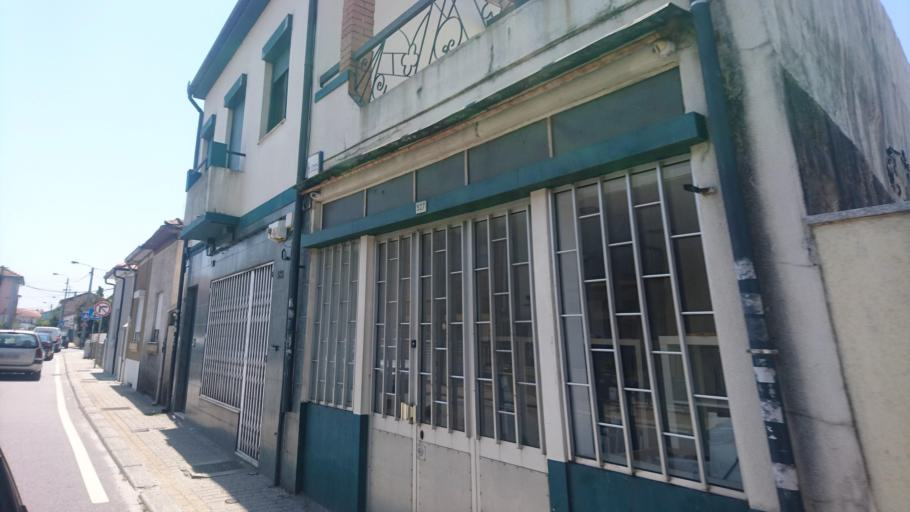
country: PT
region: Porto
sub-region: Gondomar
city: Rio Tinto
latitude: 41.1647
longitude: -8.5468
